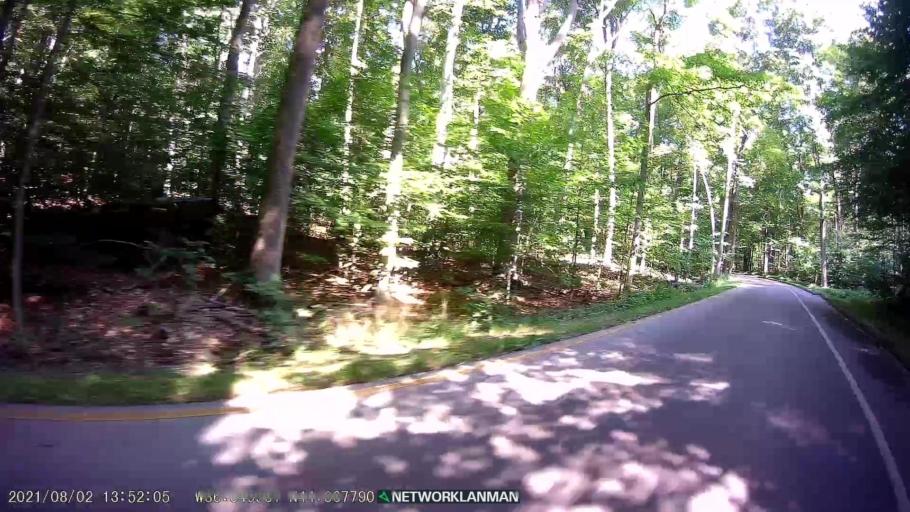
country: US
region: Michigan
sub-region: Benzie County
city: Beulah
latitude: 44.8676
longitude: -86.0494
